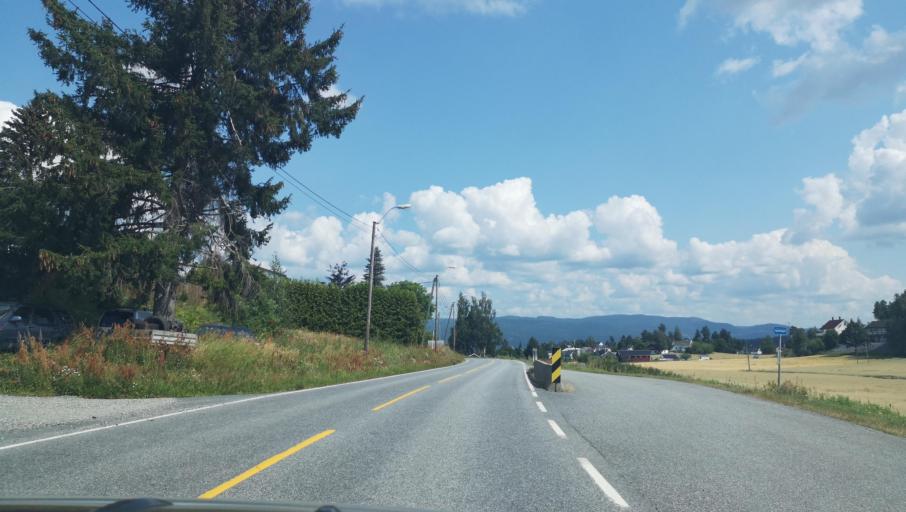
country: NO
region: Buskerud
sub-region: Ovre Eiker
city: Hokksund
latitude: 59.7304
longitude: 9.8442
